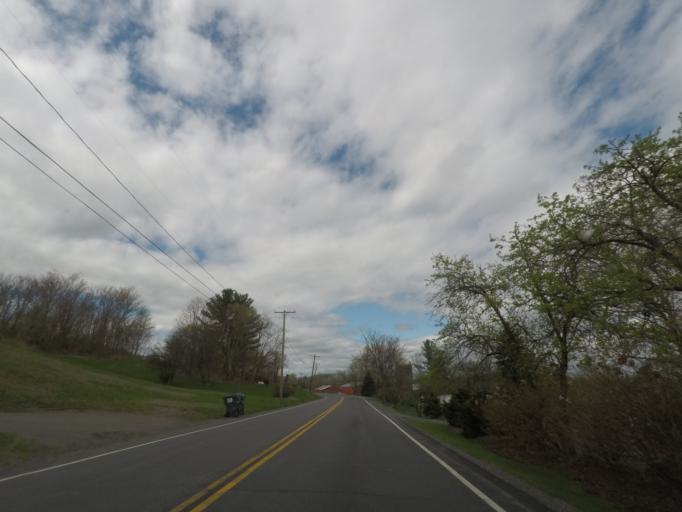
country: US
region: New York
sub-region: Columbia County
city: Valatie
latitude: 42.3892
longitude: -73.6432
